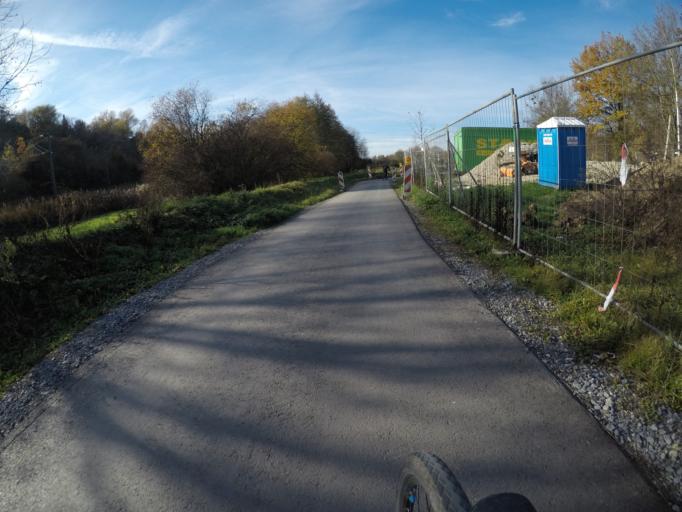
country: DE
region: Baden-Wuerttemberg
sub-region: Regierungsbezirk Stuttgart
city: Winterbach
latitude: 48.8034
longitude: 9.4540
